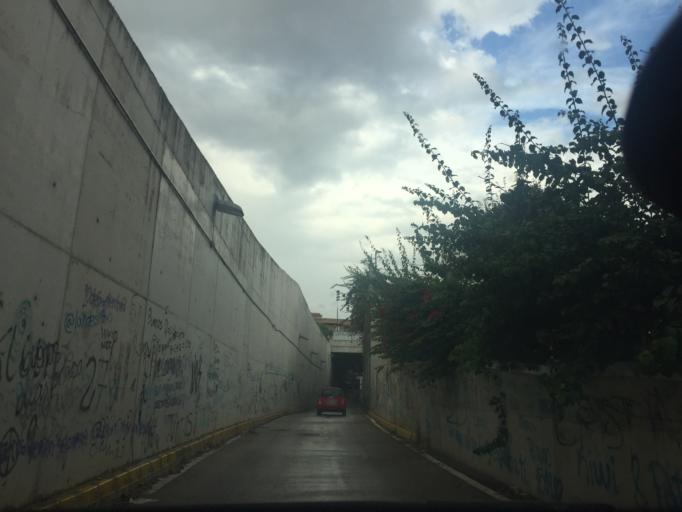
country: ES
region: Andalusia
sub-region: Provincia de Jaen
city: Jaen
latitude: 37.7770
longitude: -3.7878
